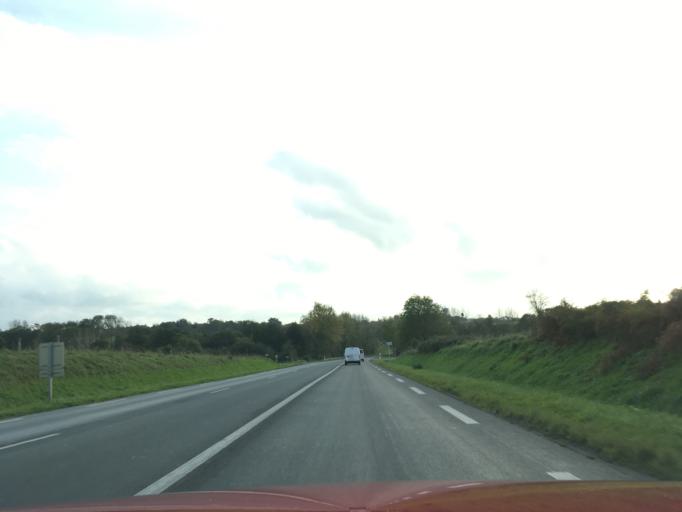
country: FR
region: Lower Normandy
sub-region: Departement de la Manche
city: Saint-Planchers
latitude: 48.8254
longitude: -1.5460
